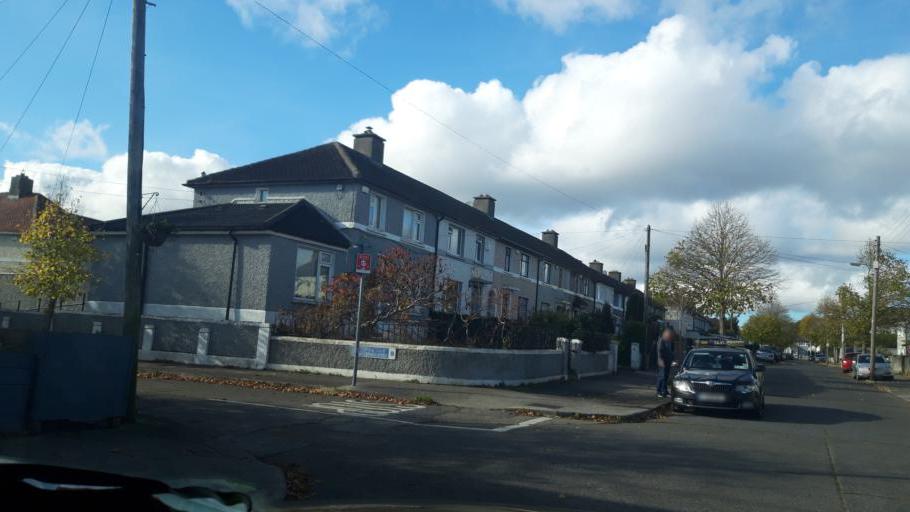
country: IE
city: Donnycarney
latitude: 53.3738
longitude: -6.2233
